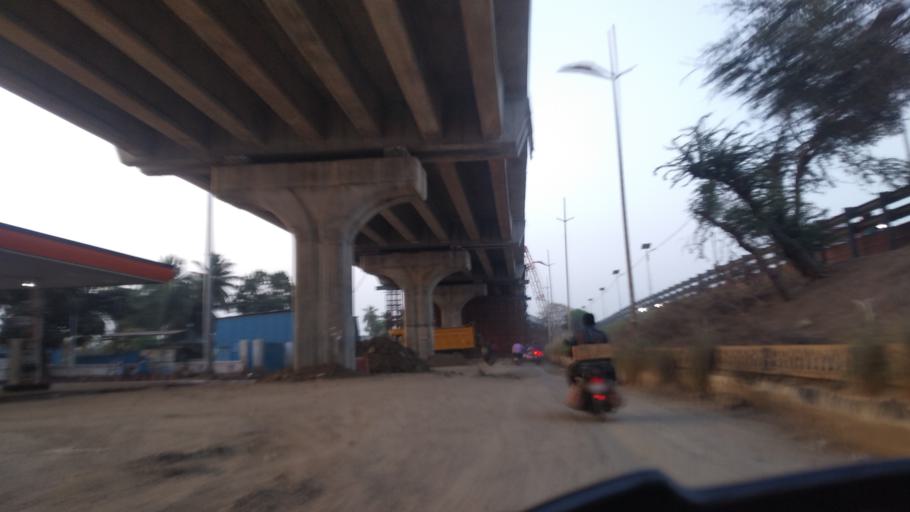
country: IN
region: Tamil Nadu
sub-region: Coimbatore
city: Coimbatore
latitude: 10.9818
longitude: 76.9614
